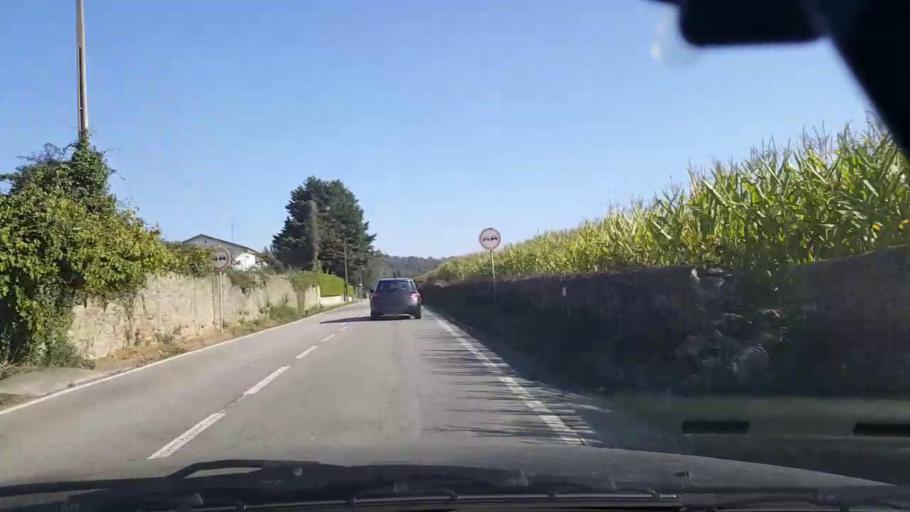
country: PT
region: Porto
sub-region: Vila do Conde
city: Arvore
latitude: 41.3294
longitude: -8.6605
